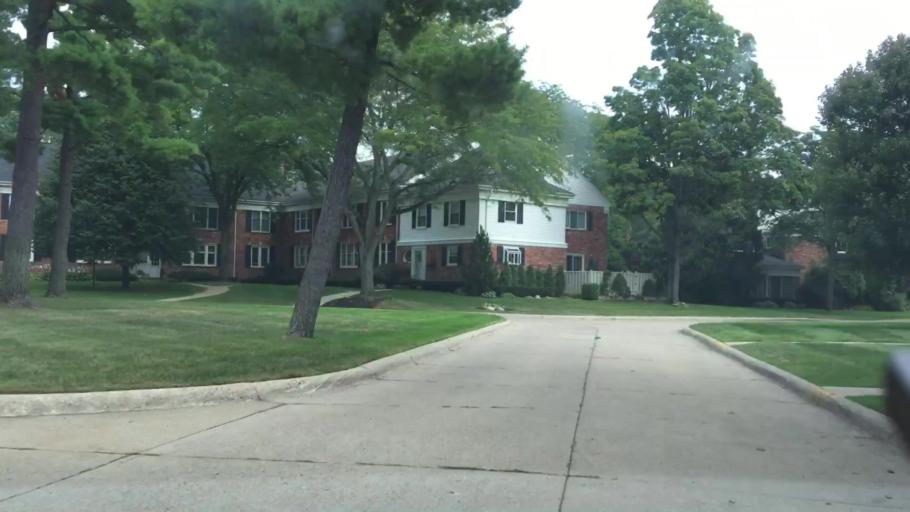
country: US
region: Michigan
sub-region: Oakland County
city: Franklin
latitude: 42.5468
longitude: -83.2890
